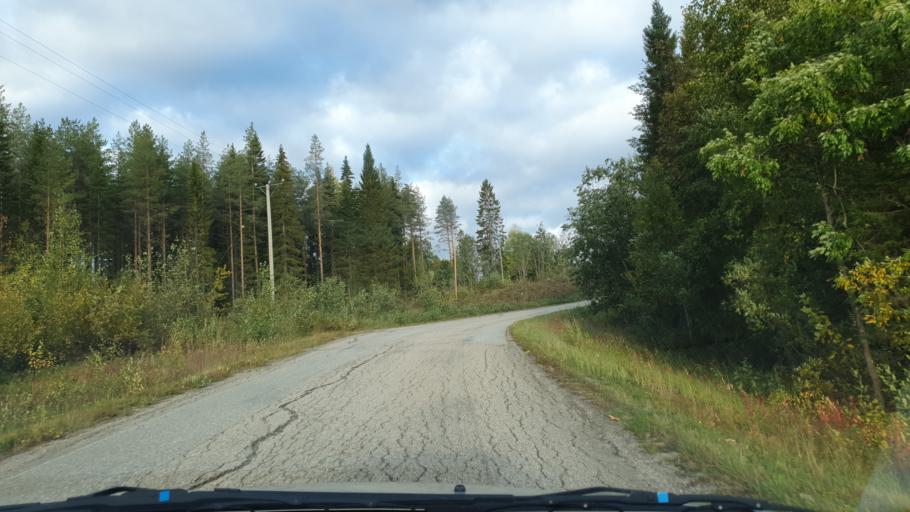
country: FI
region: North Karelia
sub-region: Pielisen Karjala
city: Lieksa
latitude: 63.9216
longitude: 30.1493
